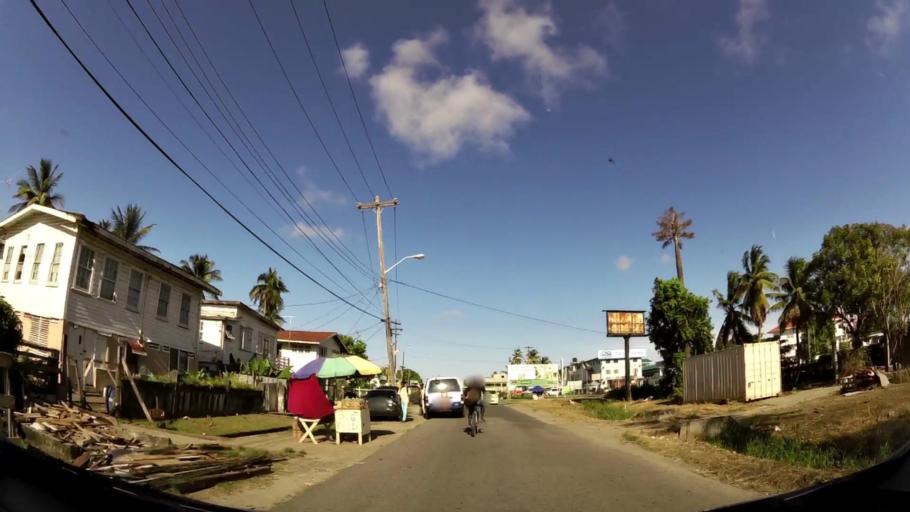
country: GY
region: Demerara-Mahaica
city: Georgetown
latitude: 6.8210
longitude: -58.1352
